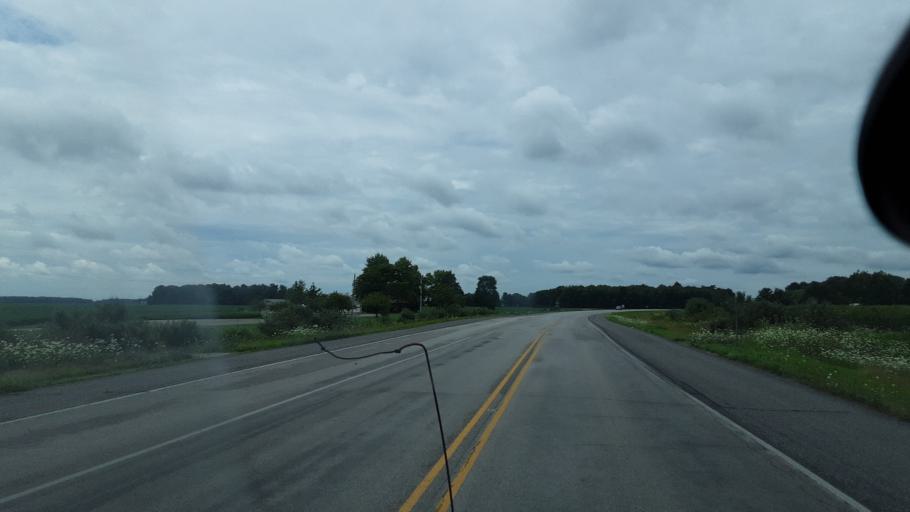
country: US
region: Indiana
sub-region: Adams County
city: Decatur
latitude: 40.8044
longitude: -84.9003
